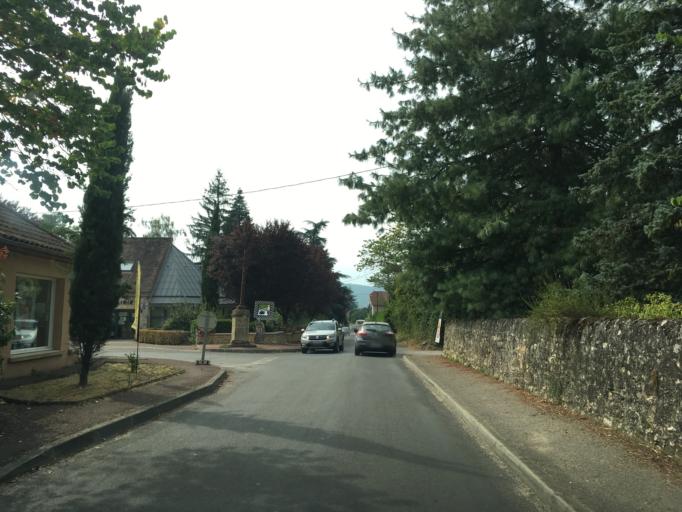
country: FR
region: Midi-Pyrenees
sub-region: Departement du Lot
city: Souillac
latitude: 44.8550
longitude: 1.5132
